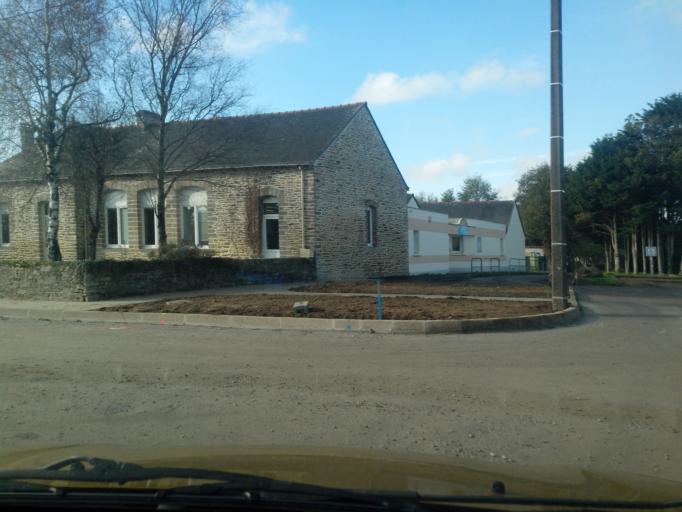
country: FR
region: Brittany
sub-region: Departement du Morbihan
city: Molac
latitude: 47.7327
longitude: -2.4356
